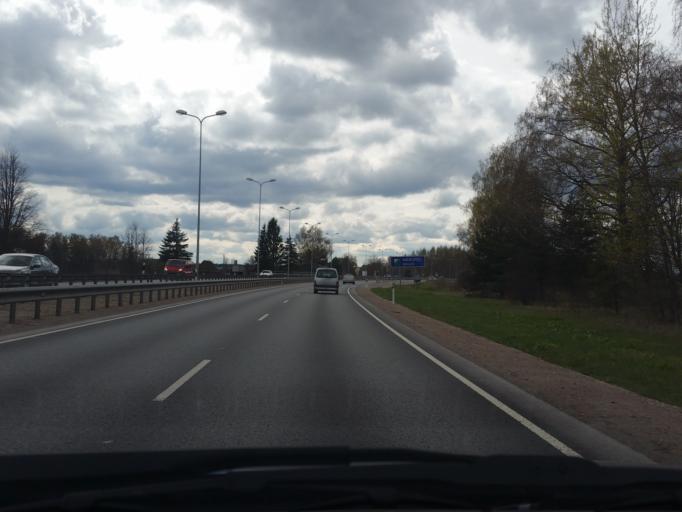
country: LV
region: Marupe
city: Marupe
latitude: 56.9242
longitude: 23.9988
